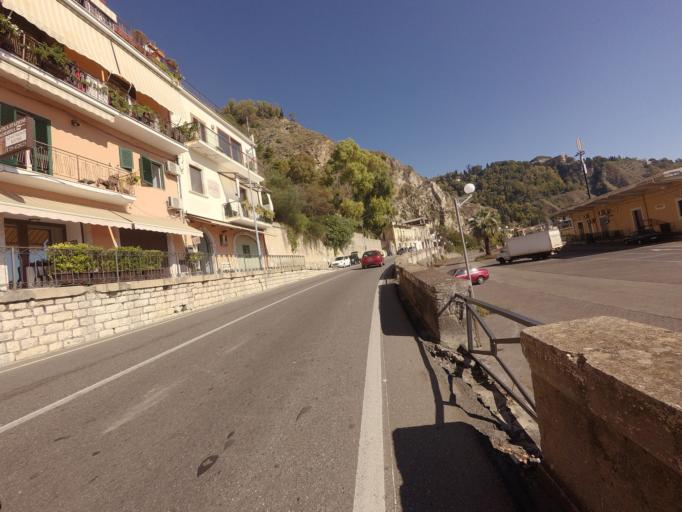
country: IT
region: Sicily
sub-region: Messina
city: Taormina
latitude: 37.8465
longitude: 15.2832
